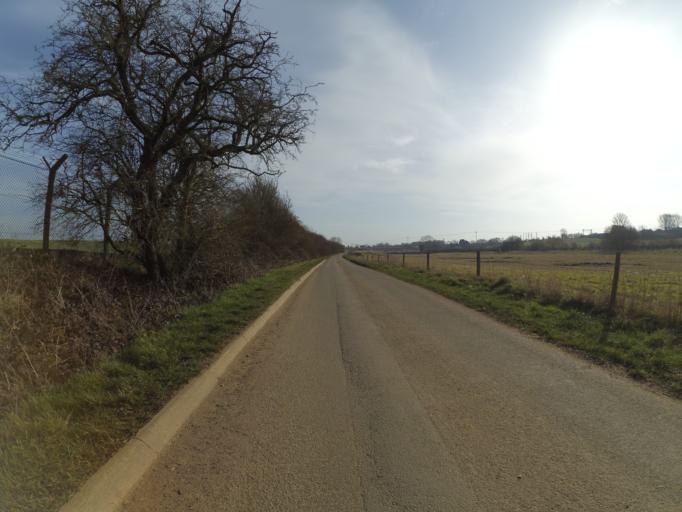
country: GB
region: England
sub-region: Warwickshire
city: Rugby
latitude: 52.3609
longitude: -1.2019
